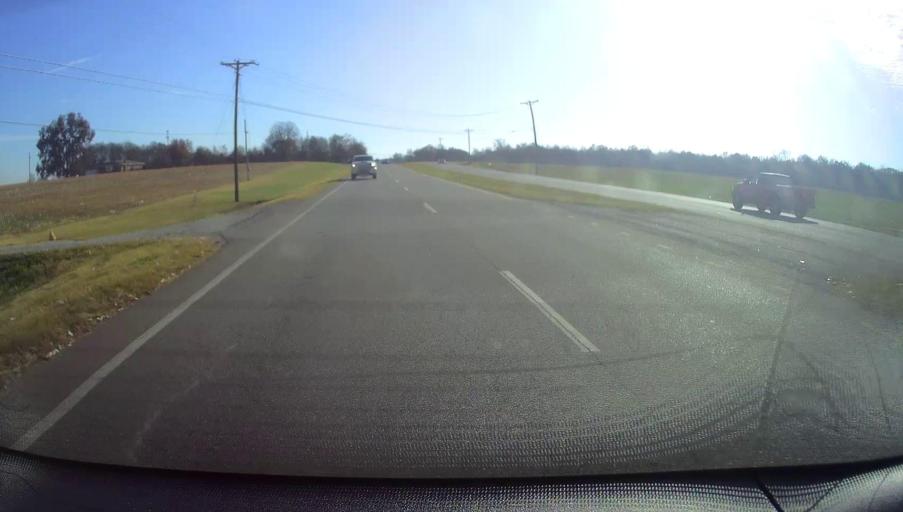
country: US
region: Alabama
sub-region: Limestone County
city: Athens
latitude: 34.7440
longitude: -86.9571
